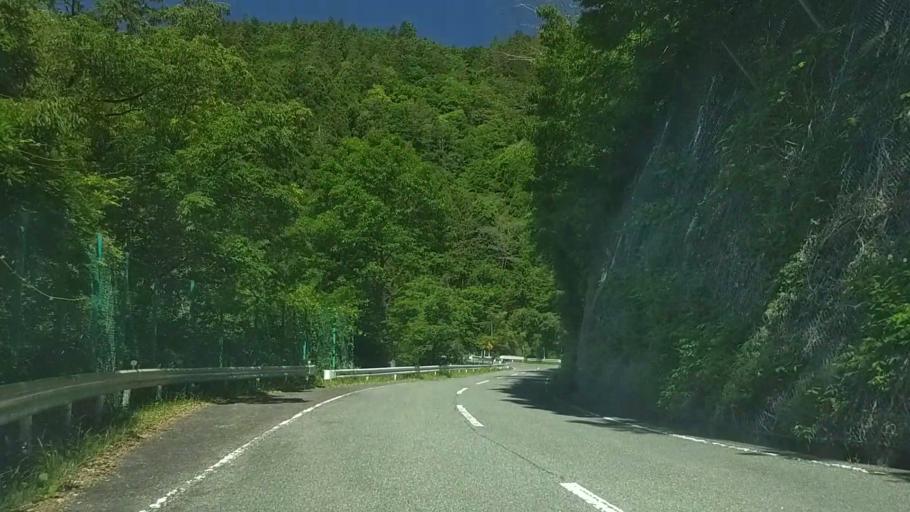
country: JP
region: Yamanashi
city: Ryuo
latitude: 35.5098
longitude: 138.4061
